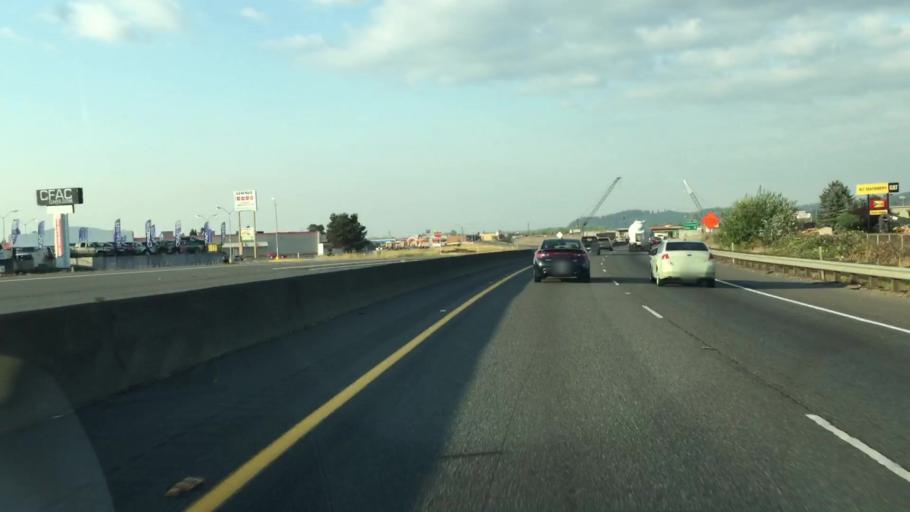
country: US
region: Washington
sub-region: Lewis County
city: Chehalis
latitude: 46.6721
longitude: -122.9764
